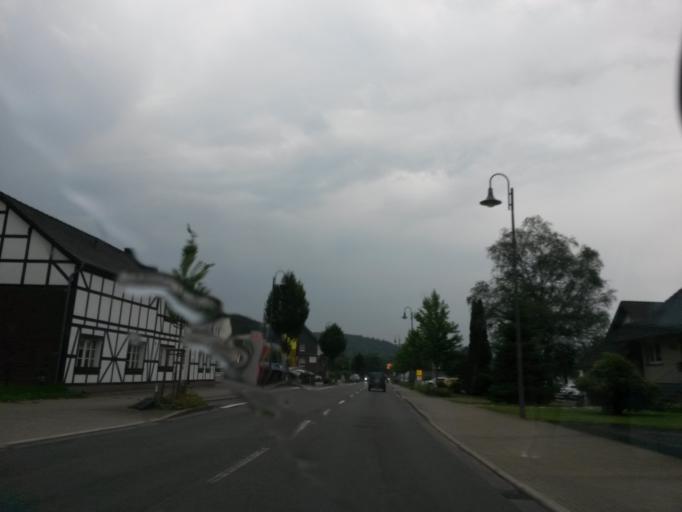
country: DE
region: North Rhine-Westphalia
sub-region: Regierungsbezirk Koln
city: Overath
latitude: 50.9623
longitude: 7.3198
